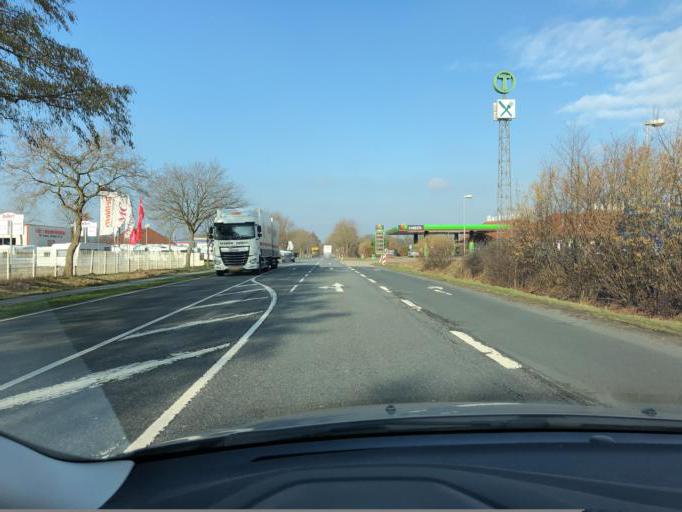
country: DE
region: Lower Saxony
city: Westerstede
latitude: 53.2867
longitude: 7.8946
